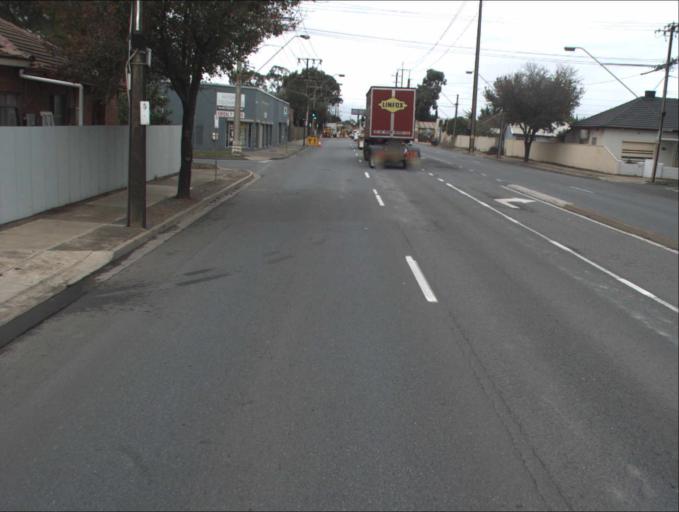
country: AU
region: South Australia
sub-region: Charles Sturt
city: Woodville
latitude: -34.8776
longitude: 138.5715
